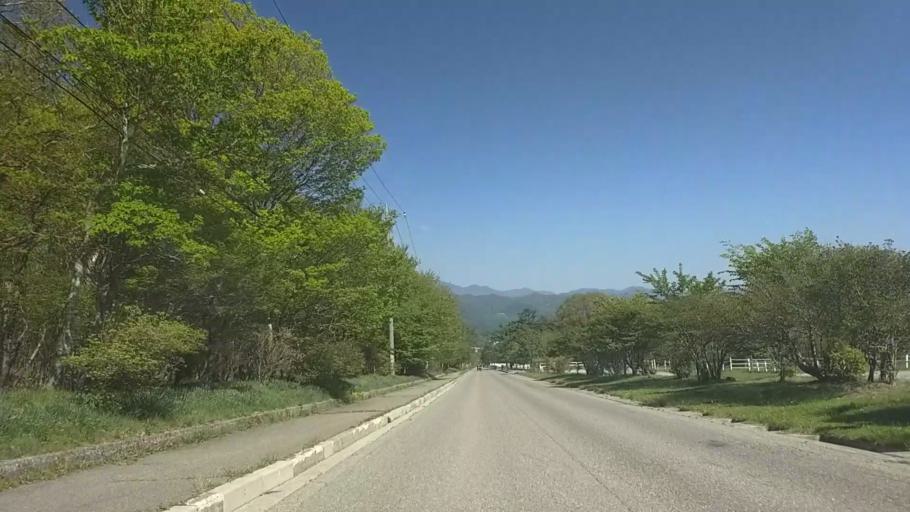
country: JP
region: Yamanashi
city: Nirasaki
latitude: 35.9245
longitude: 138.4221
